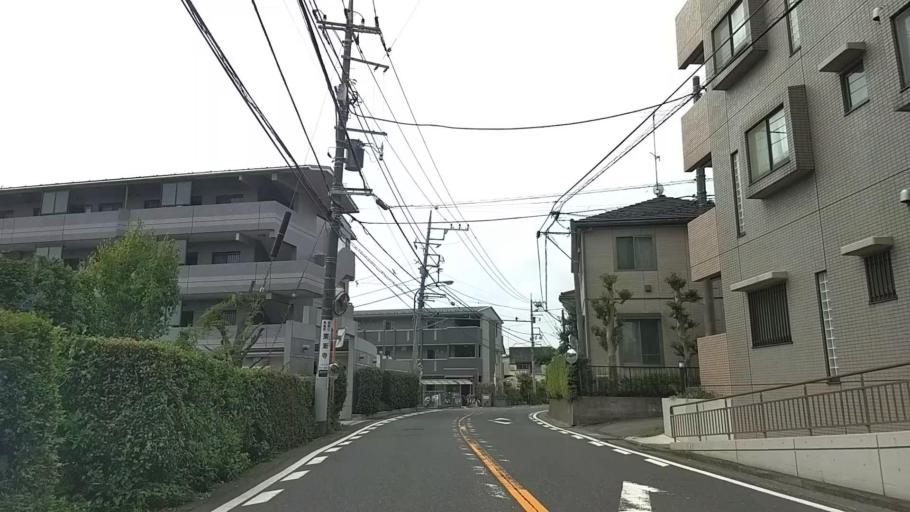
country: JP
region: Kanagawa
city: Yokohama
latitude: 35.5155
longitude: 139.5584
